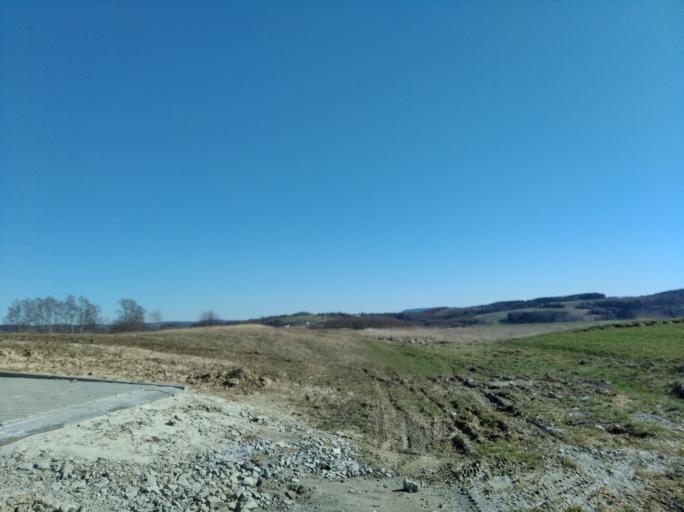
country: PL
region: Subcarpathian Voivodeship
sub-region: Powiat strzyzowski
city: Wisniowa
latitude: 49.9165
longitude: 21.6803
